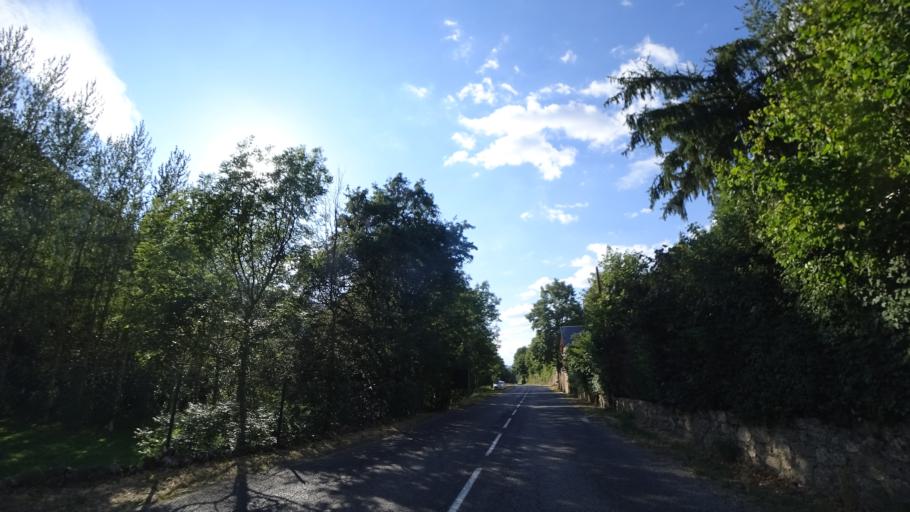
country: FR
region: Languedoc-Roussillon
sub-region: Departement de la Lozere
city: La Canourgue
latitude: 44.4179
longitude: 3.2308
